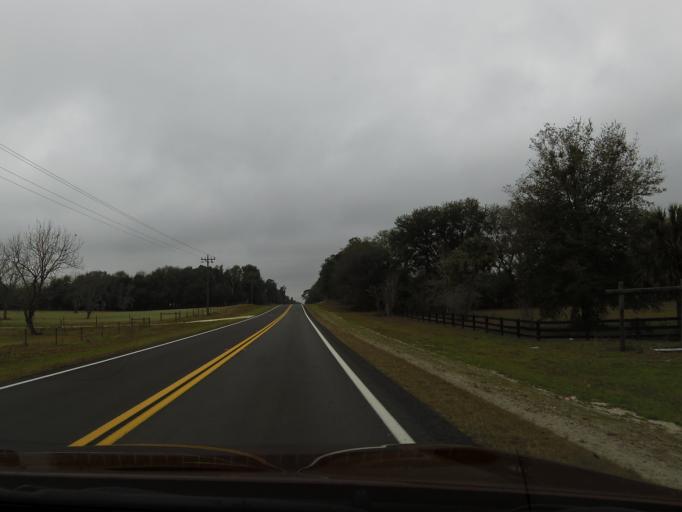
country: US
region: Florida
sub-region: Gilchrist County
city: Trenton
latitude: 29.7962
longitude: -82.8427
